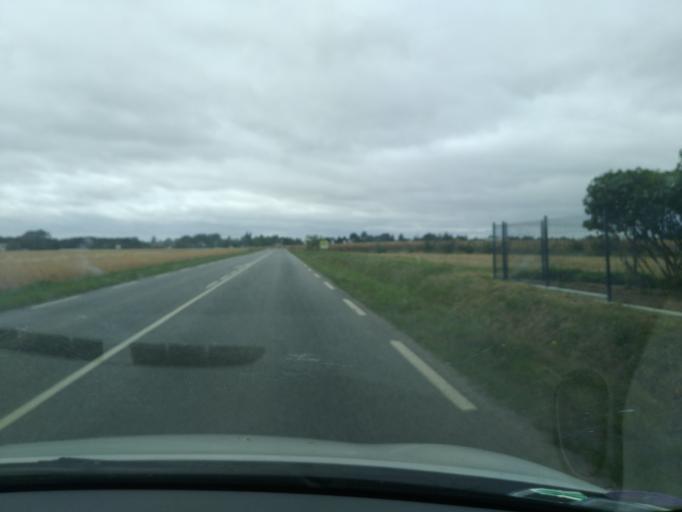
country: FR
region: Ile-de-France
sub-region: Departement des Yvelines
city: Les Alluets-le-Roi
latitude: 48.9147
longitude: 1.9321
